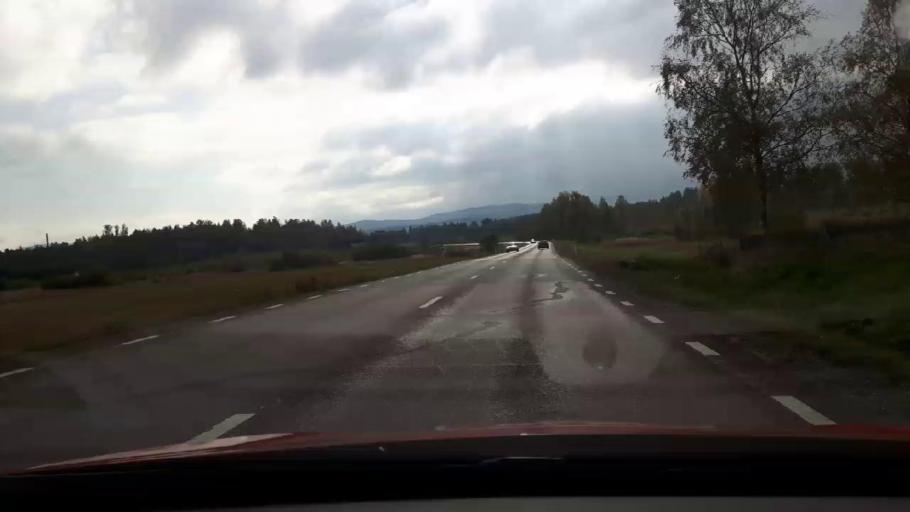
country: SE
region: Gaevleborg
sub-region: Bollnas Kommun
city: Kilafors
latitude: 61.2430
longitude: 16.5504
